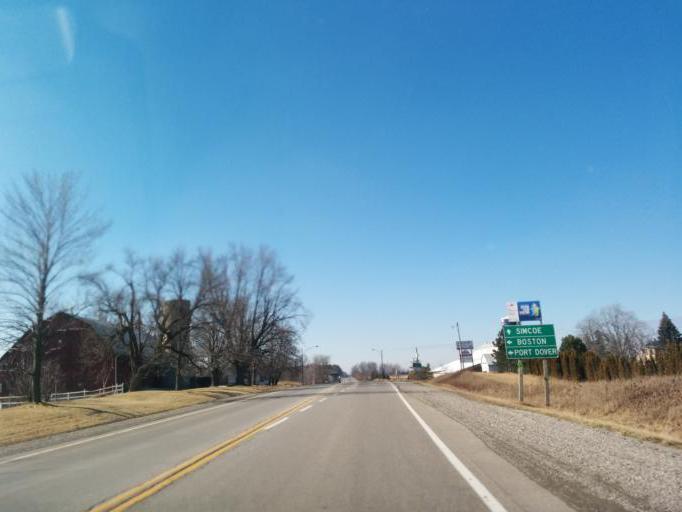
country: CA
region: Ontario
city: Brantford
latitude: 43.0388
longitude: -80.2850
